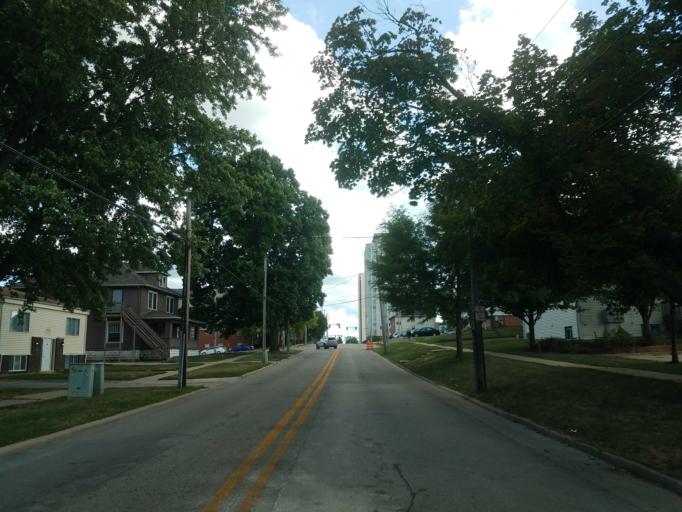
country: US
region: Illinois
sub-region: McLean County
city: Normal
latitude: 40.5130
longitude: -88.9873
